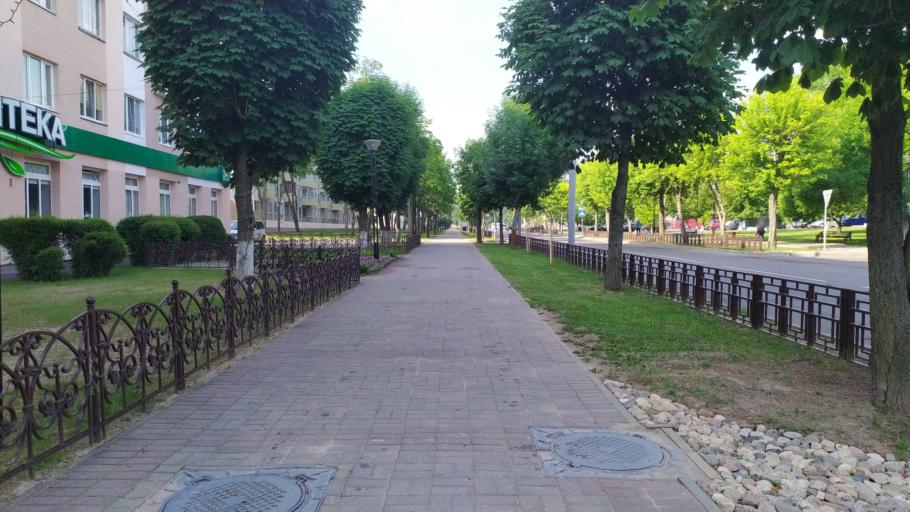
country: BY
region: Vitebsk
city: Navapolatsk
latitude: 55.5339
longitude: 28.6480
